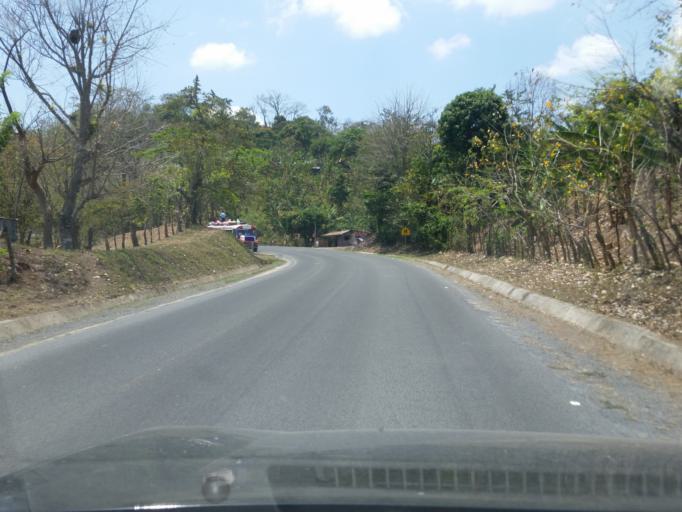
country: NI
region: Matagalpa
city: Muy Muy
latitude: 12.6091
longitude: -85.5393
